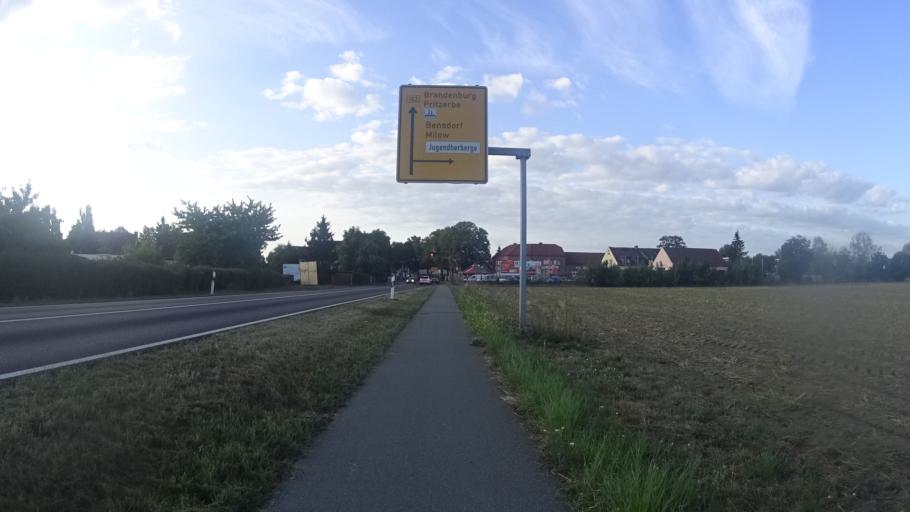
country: DE
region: Brandenburg
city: Premnitz
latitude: 52.5378
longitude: 12.3271
